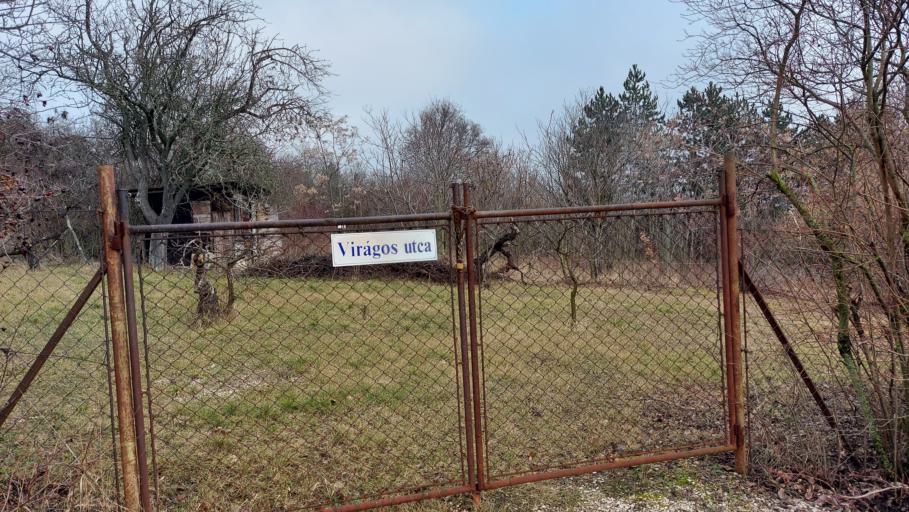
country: HU
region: Pest
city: Budaors
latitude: 47.4722
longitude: 18.9575
